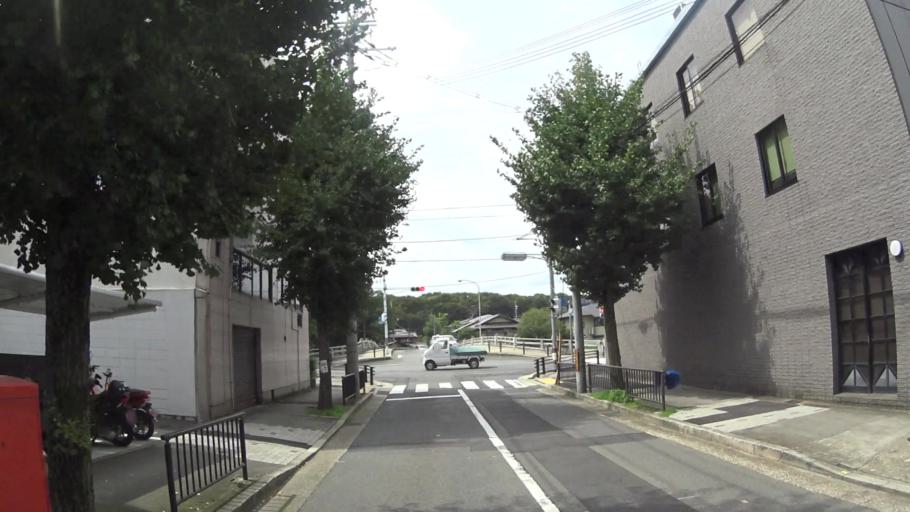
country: JP
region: Kyoto
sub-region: Kyoto-shi
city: Kamigyo-ku
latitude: 35.0339
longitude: 135.7750
